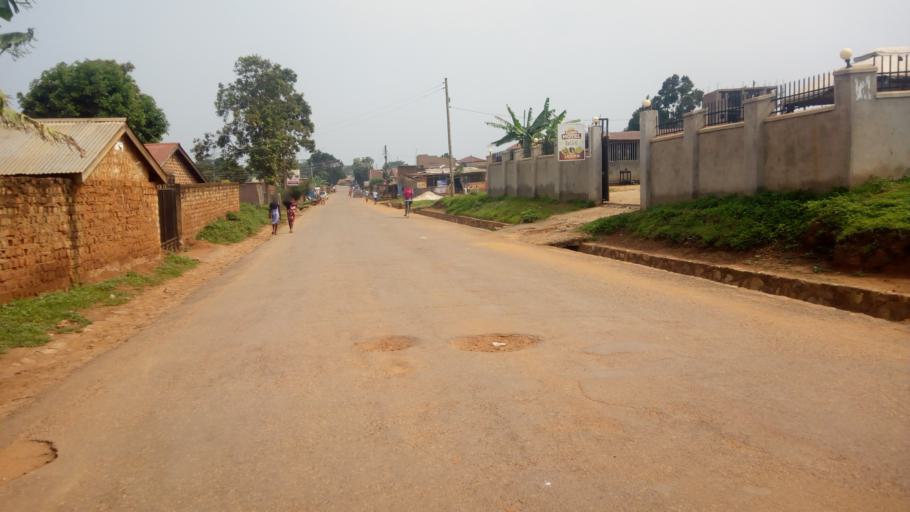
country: UG
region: Central Region
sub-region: Wakiso District
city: Kireka
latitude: 0.3058
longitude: 32.6516
